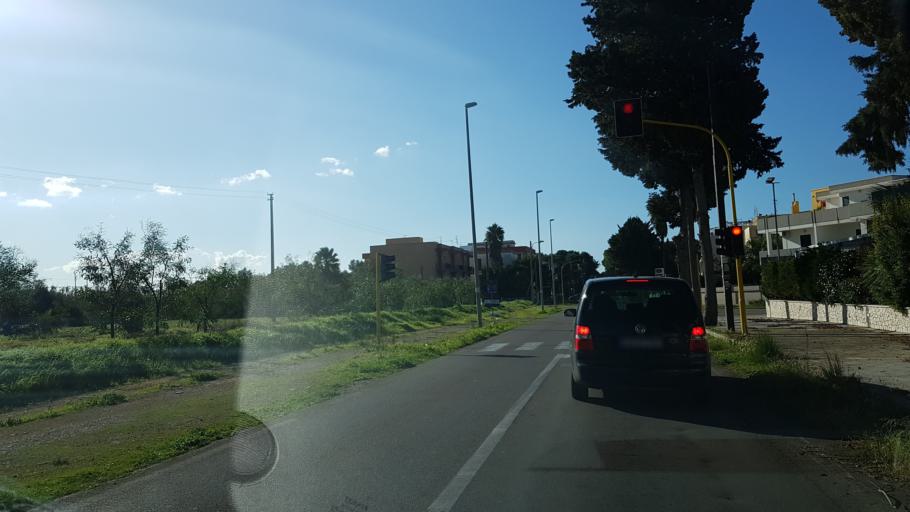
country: IT
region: Apulia
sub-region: Provincia di Lecce
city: Gallipoli
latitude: 40.0858
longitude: 18.0138
